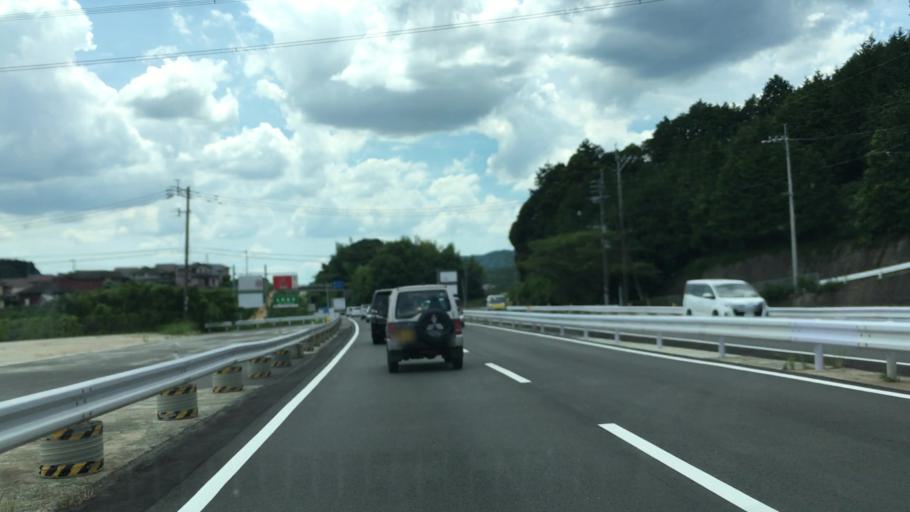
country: JP
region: Fukuoka
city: Chikushino-shi
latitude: 33.4404
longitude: 130.5268
